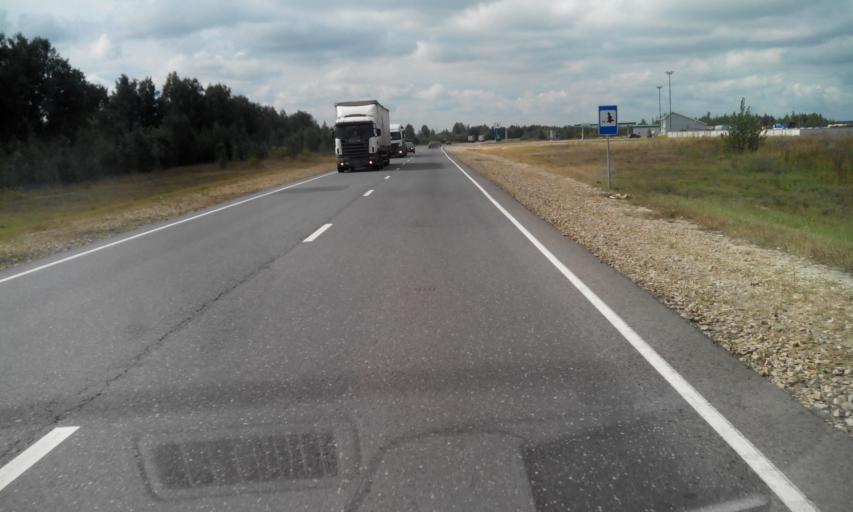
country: RU
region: Ulyanovsk
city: Nikolayevka
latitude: 53.1285
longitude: 46.9983
